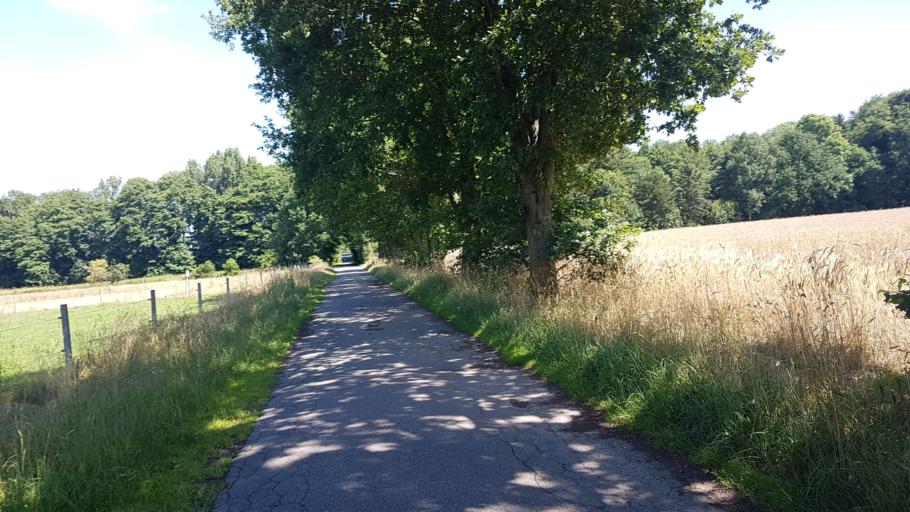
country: DE
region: Lower Saxony
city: Rullstorf
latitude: 53.2820
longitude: 10.5170
